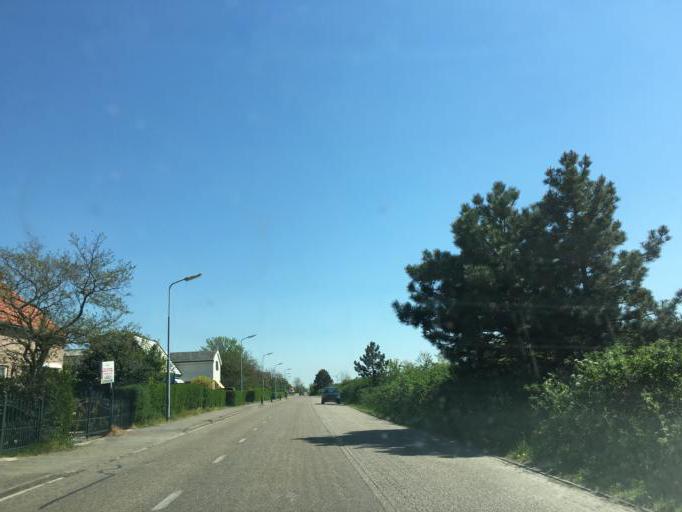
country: NL
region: North Holland
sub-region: Gemeente Den Helder
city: Den Helder
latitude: 52.8608
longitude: 4.7192
